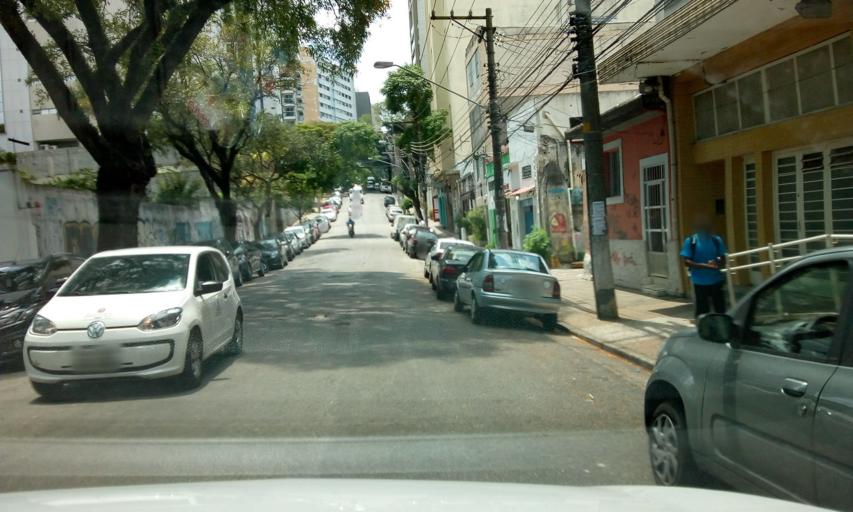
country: BR
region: Sao Paulo
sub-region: Sao Paulo
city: Sao Paulo
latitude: -23.5728
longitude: -46.6392
